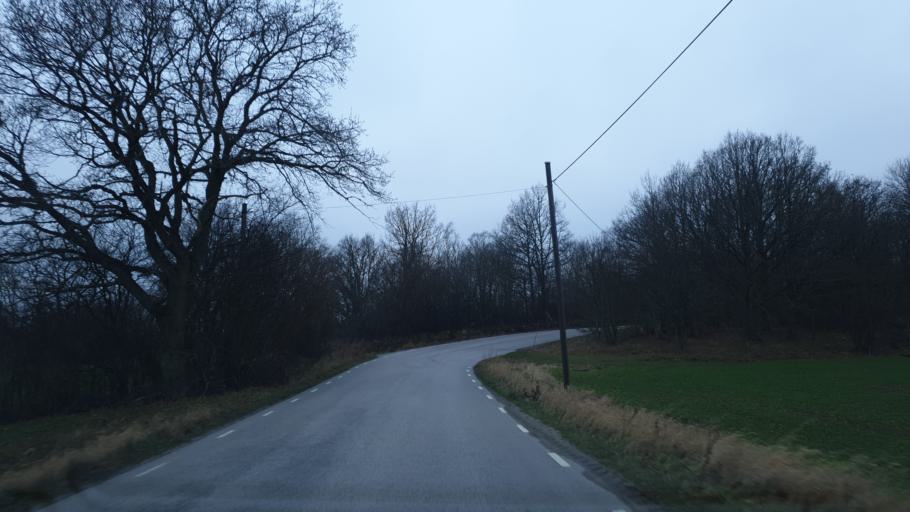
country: SE
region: Blekinge
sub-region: Karlskrona Kommun
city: Rodeby
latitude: 56.2018
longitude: 15.6861
